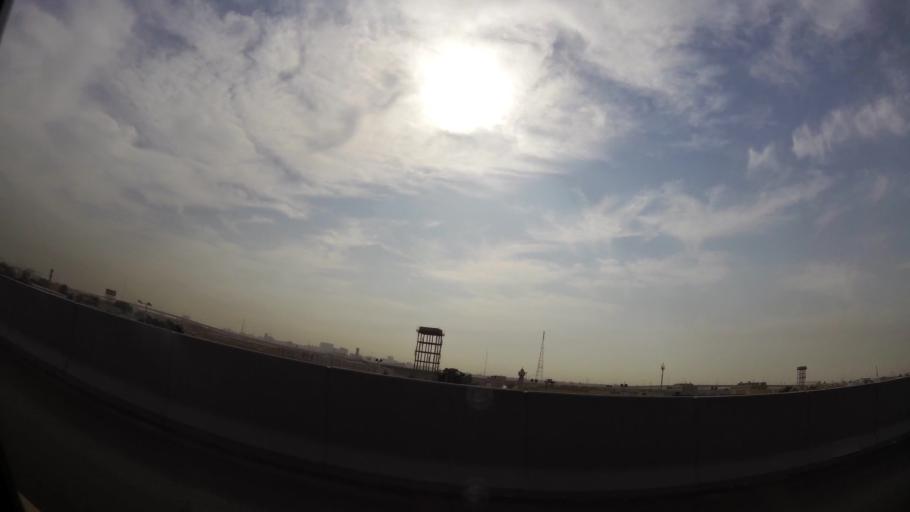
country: KW
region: Al Asimah
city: Ar Rabiyah
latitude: 29.3194
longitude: 47.8844
